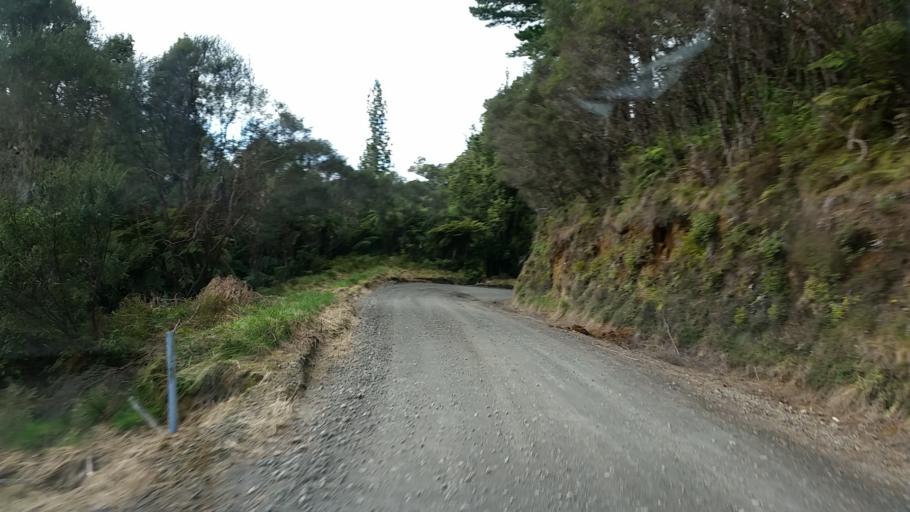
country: NZ
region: Taranaki
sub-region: New Plymouth District
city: Waitara
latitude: -39.1577
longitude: 174.5533
